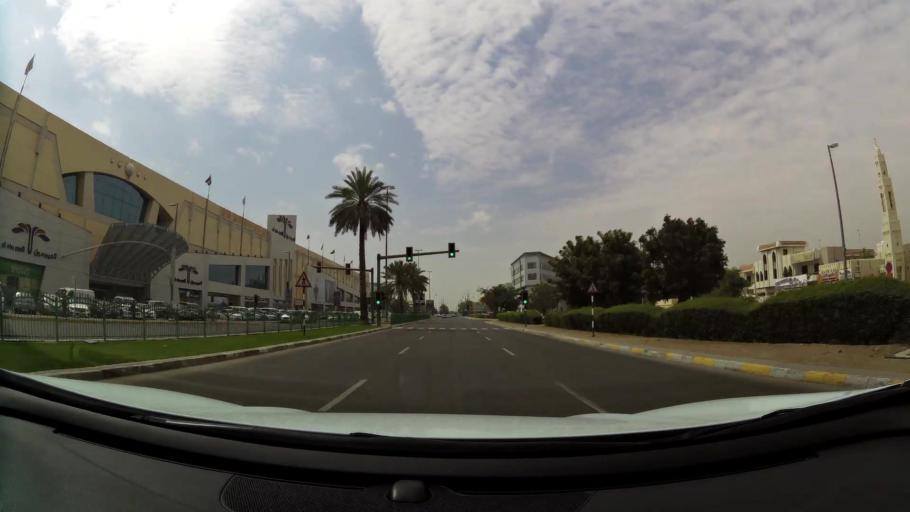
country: OM
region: Al Buraimi
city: Al Buraymi
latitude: 24.2234
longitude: 55.7820
